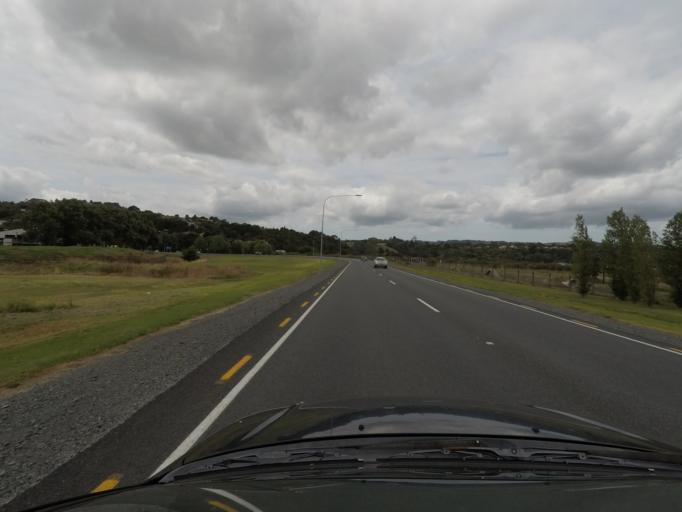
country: NZ
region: Northland
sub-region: Whangarei
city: Whangarei
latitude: -35.7345
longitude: 174.3416
